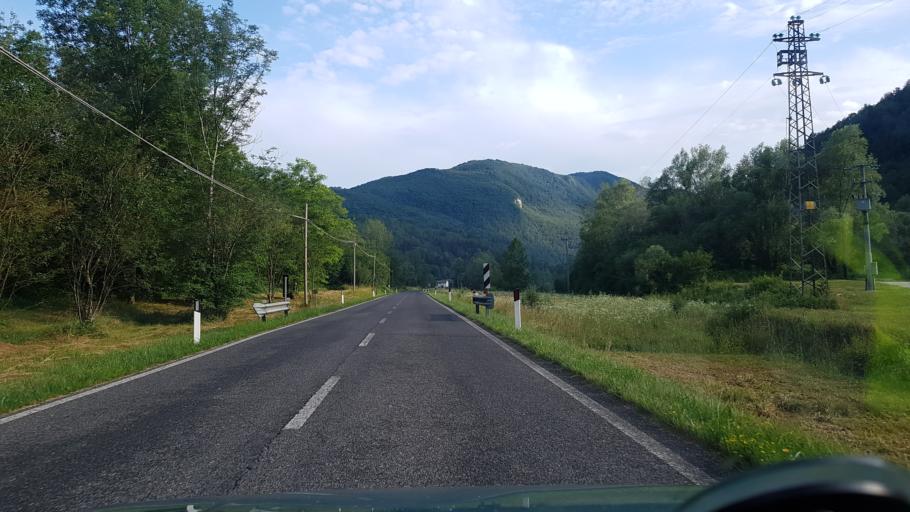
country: IT
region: Friuli Venezia Giulia
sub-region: Provincia di Udine
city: Lusevera
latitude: 46.2724
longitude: 13.2599
